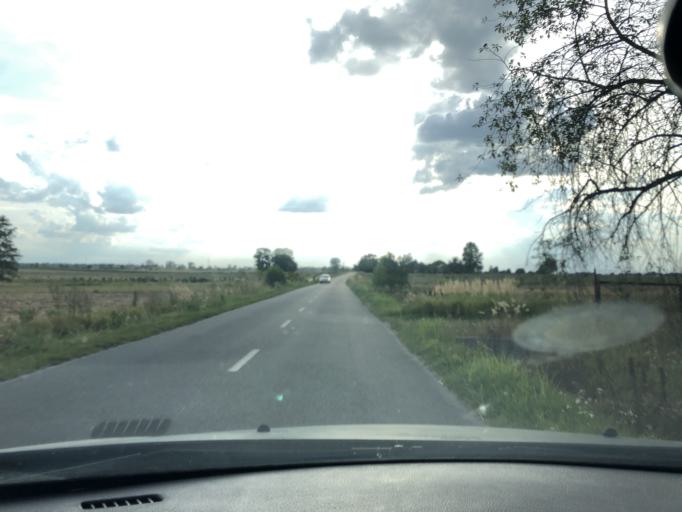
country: PL
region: Lodz Voivodeship
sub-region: Powiat wieruszowski
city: Walichnowy
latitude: 51.2462
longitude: 18.3879
